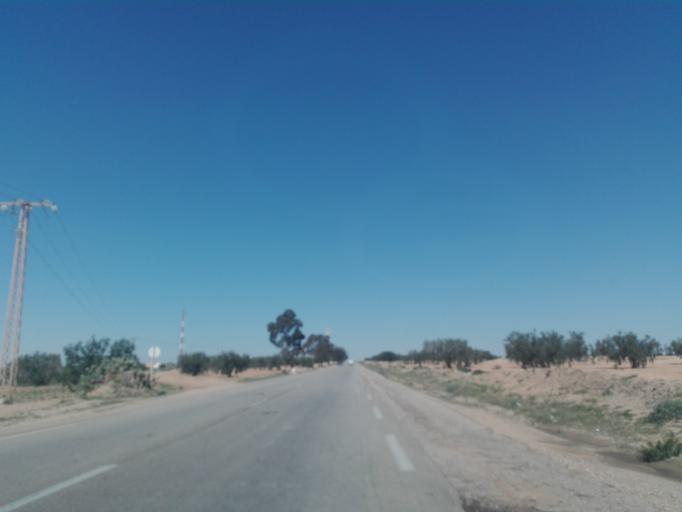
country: TN
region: Safaqis
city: Bi'r `Ali Bin Khalifah
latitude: 34.7539
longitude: 10.3362
